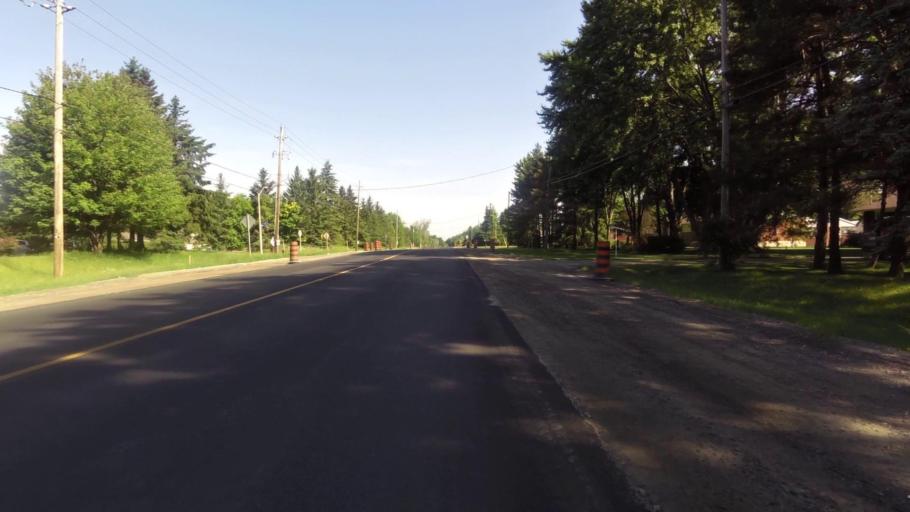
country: CA
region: Ontario
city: Ottawa
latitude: 45.2509
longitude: -75.5905
